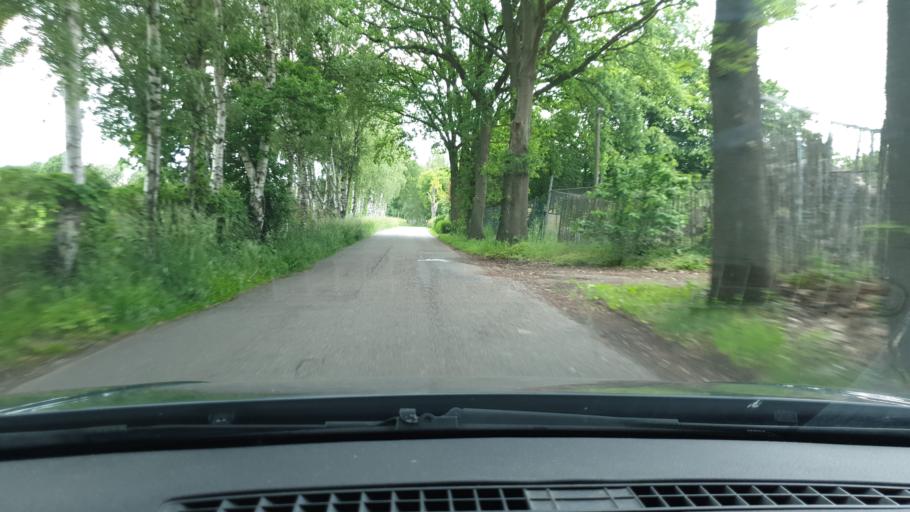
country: BE
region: Flanders
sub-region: Provincie Antwerpen
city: Geel
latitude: 51.1330
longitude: 4.9776
